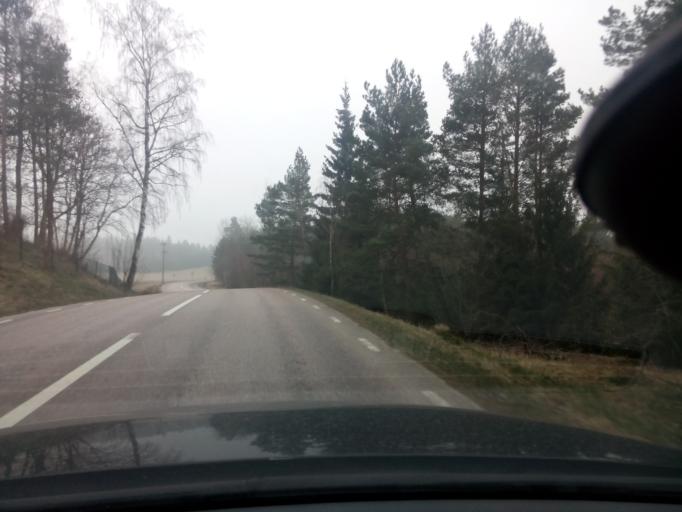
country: SE
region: Soedermanland
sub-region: Nykopings Kommun
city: Nykoping
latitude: 58.9113
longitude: 17.0951
